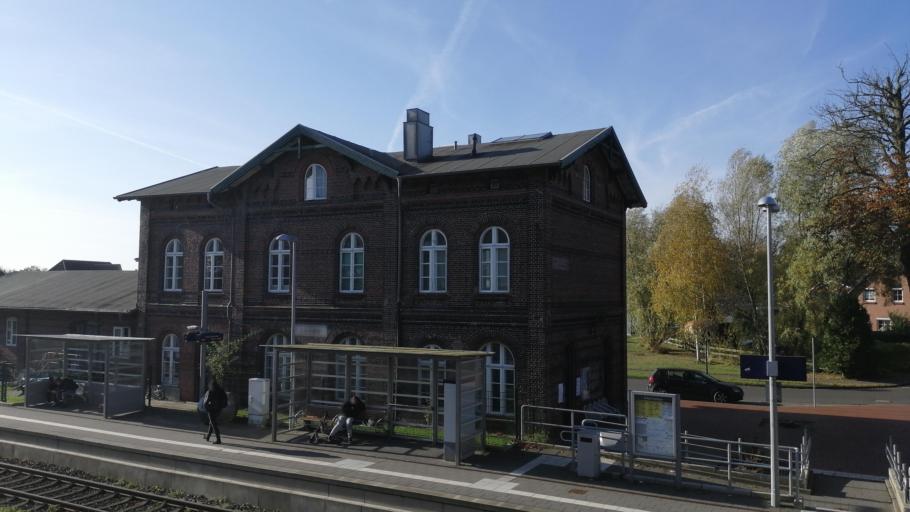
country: DE
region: Schleswig-Holstein
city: Lehe
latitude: 54.3312
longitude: 9.0308
